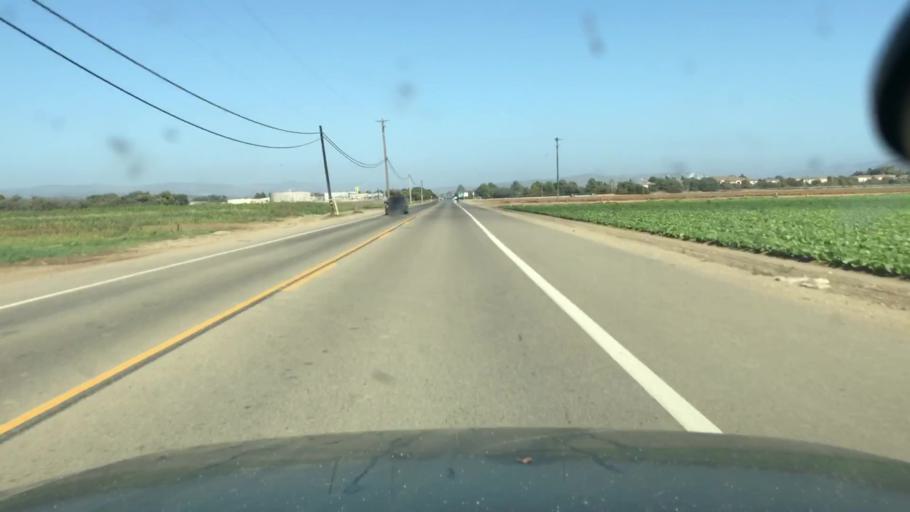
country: US
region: California
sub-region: Santa Barbara County
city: Lompoc
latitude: 34.6612
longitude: -120.4899
